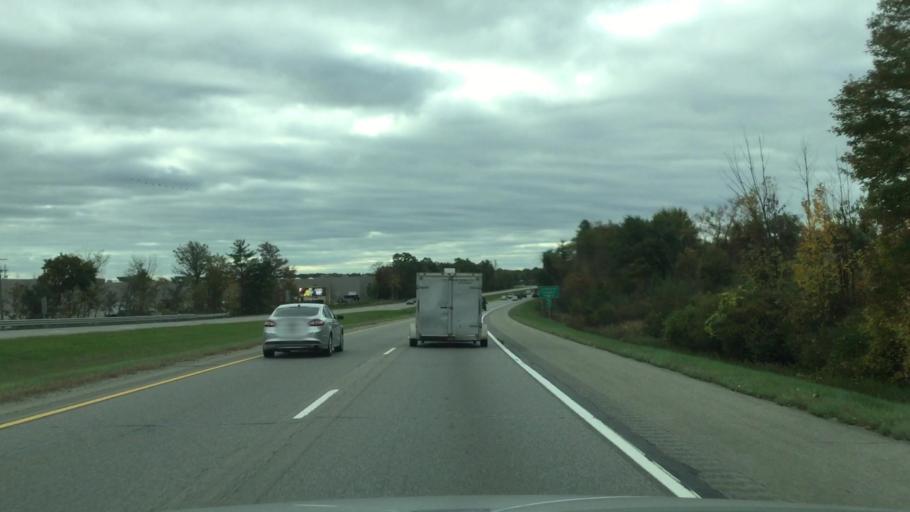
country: US
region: Michigan
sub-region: Macomb County
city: Shelby
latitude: 42.6822
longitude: -83.0158
